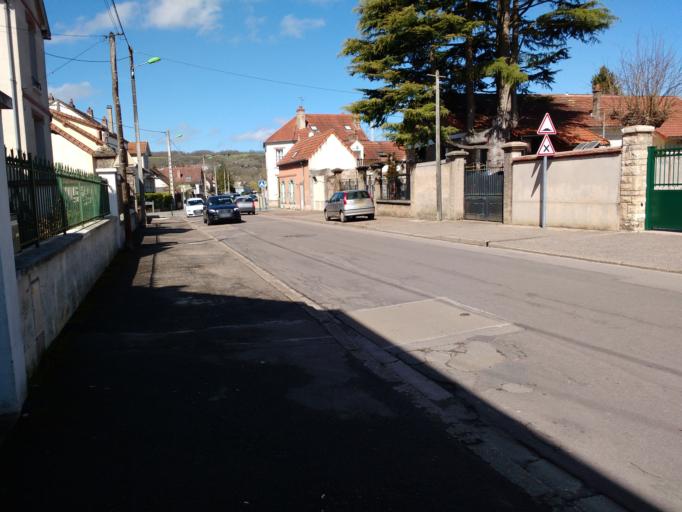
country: FR
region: Bourgogne
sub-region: Departement de l'Yonne
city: Sens
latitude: 48.1913
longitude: 3.2762
